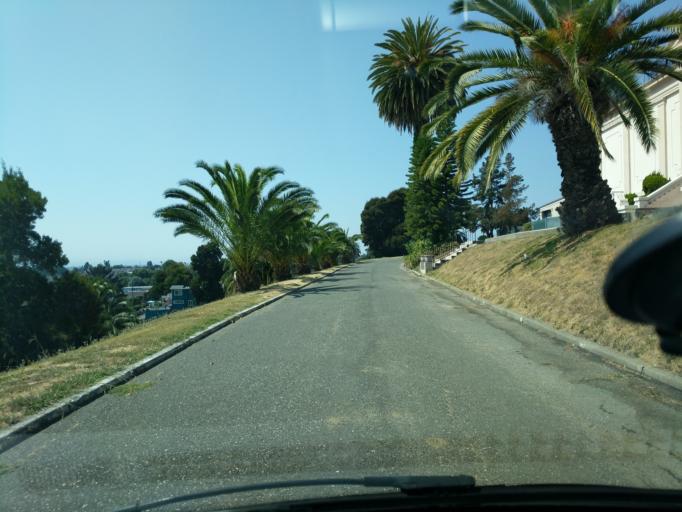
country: US
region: California
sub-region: Alameda County
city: San Leandro
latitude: 37.7710
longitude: -122.1780
